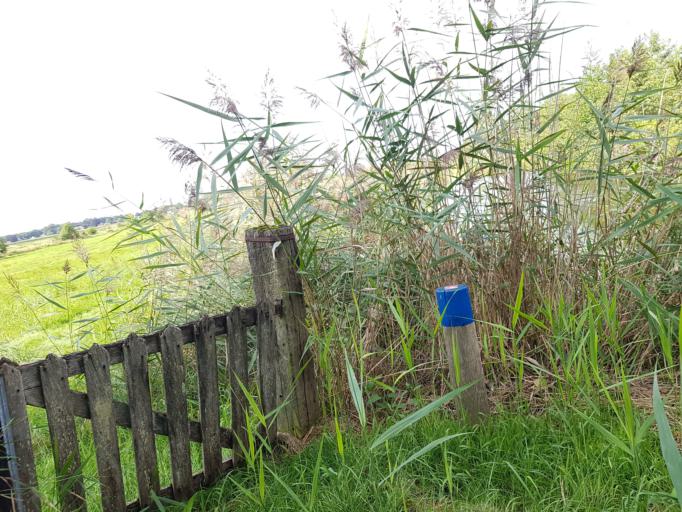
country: NL
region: Groningen
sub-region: Gemeente Hoogezand-Sappemeer
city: Hoogezand
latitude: 53.2076
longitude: 6.7439
